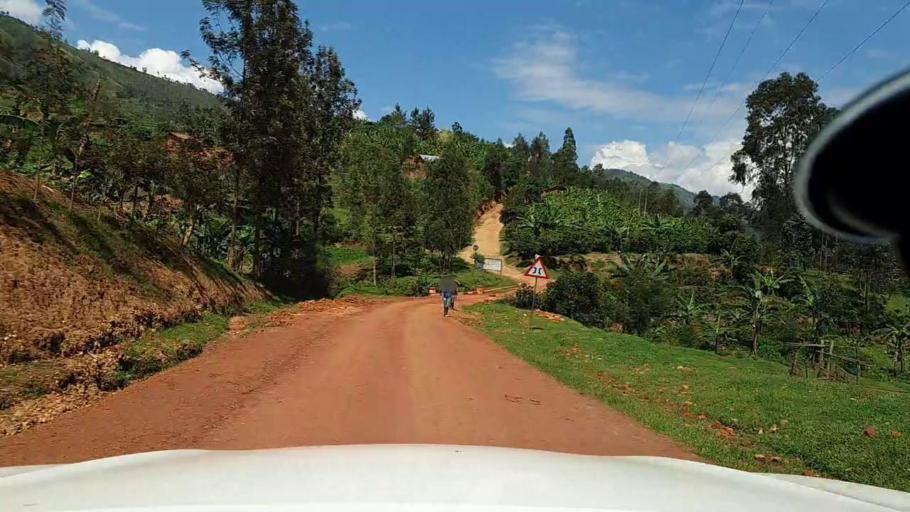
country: RW
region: Kigali
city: Kigali
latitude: -1.7858
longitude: 29.8820
